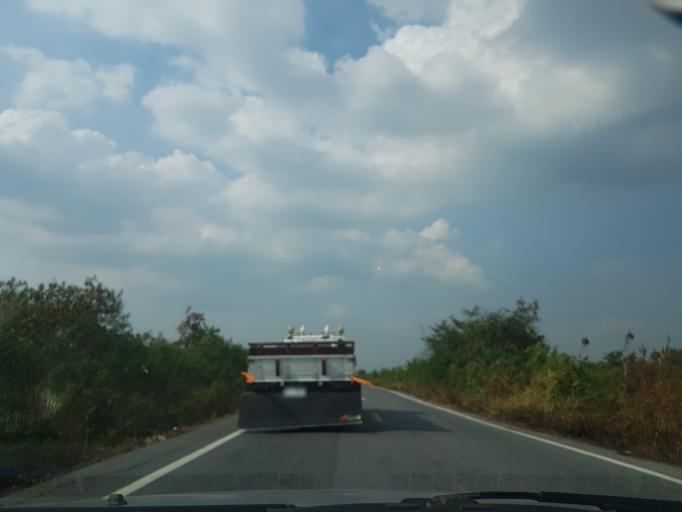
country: TH
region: Phra Nakhon Si Ayutthaya
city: Phachi
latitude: 14.4515
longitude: 100.7608
